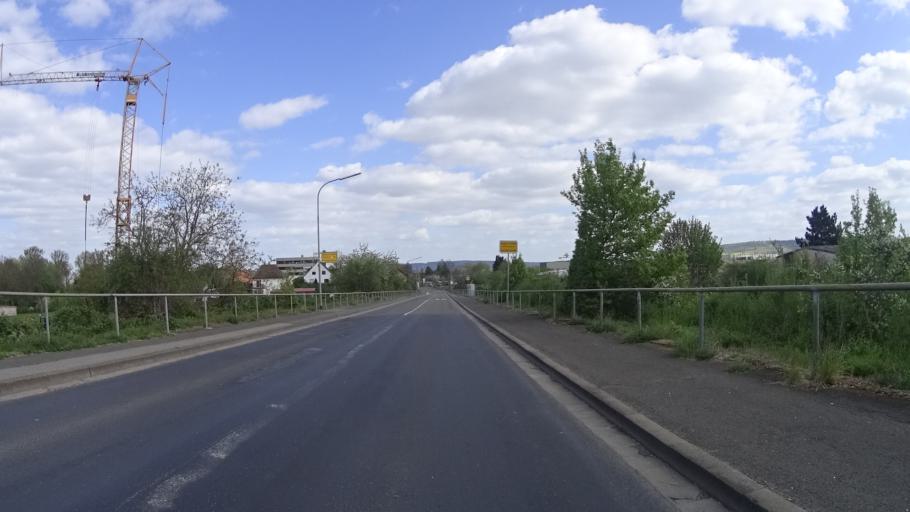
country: DE
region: Hesse
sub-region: Regierungsbezirk Darmstadt
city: Rudesheim am Rhein
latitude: 49.9680
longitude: 7.9470
